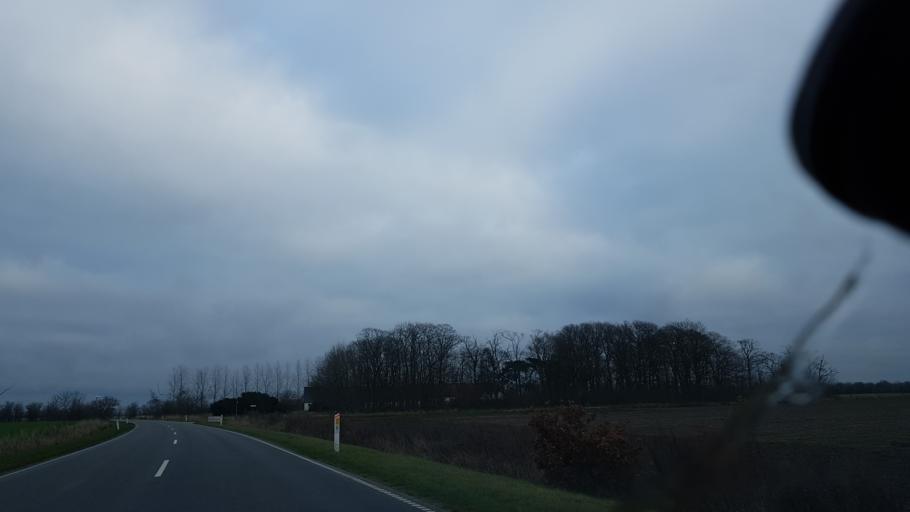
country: DK
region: South Denmark
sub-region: Tonder Kommune
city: Toftlund
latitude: 55.1915
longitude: 9.1049
